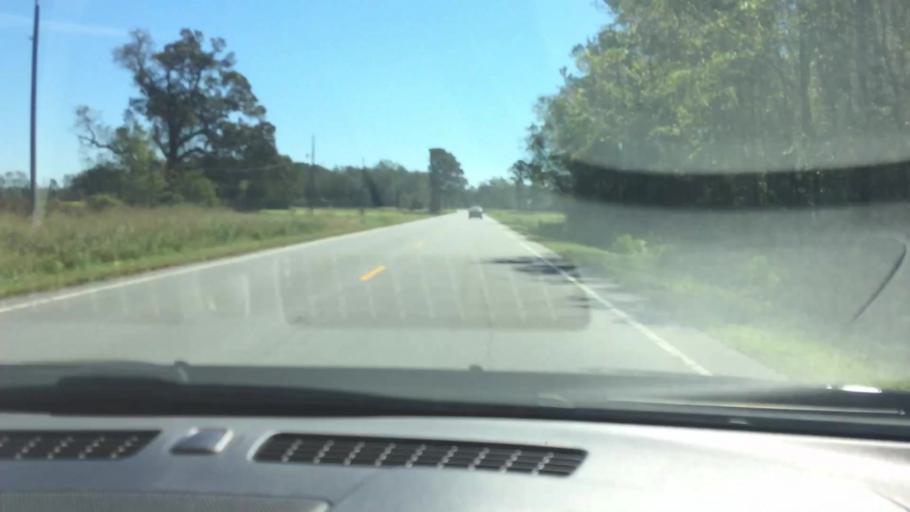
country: US
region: North Carolina
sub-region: Pitt County
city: Grifton
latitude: 35.3592
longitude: -77.3434
